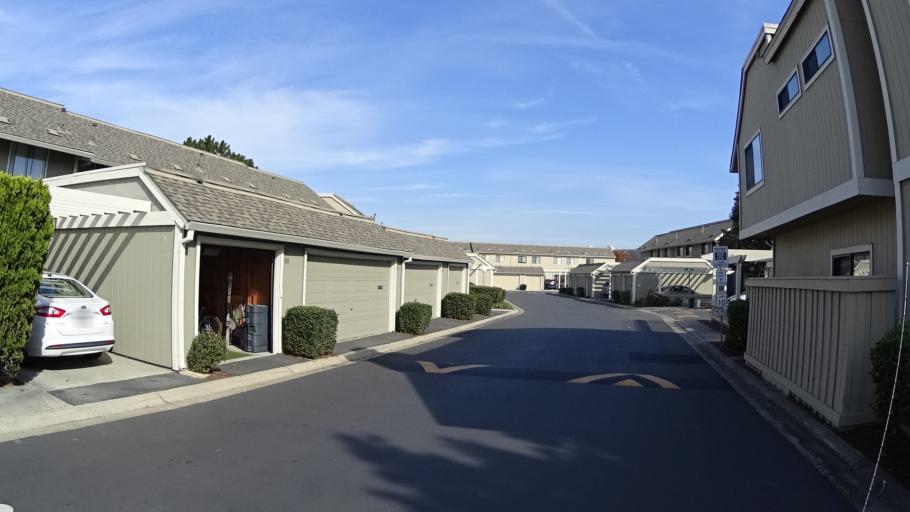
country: US
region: California
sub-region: San Mateo County
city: Foster City
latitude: 37.5466
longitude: -122.2727
